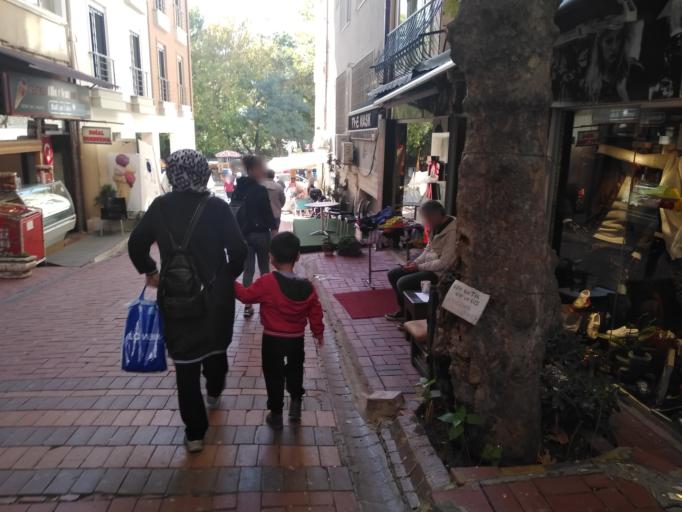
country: TR
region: Istanbul
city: Maltepe
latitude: 40.9218
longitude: 29.1284
